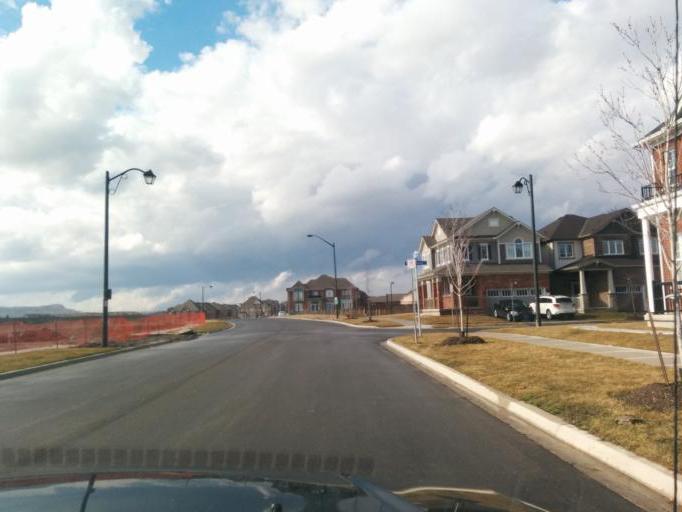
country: CA
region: Ontario
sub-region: Halton
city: Milton
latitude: 43.4909
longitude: -79.8672
